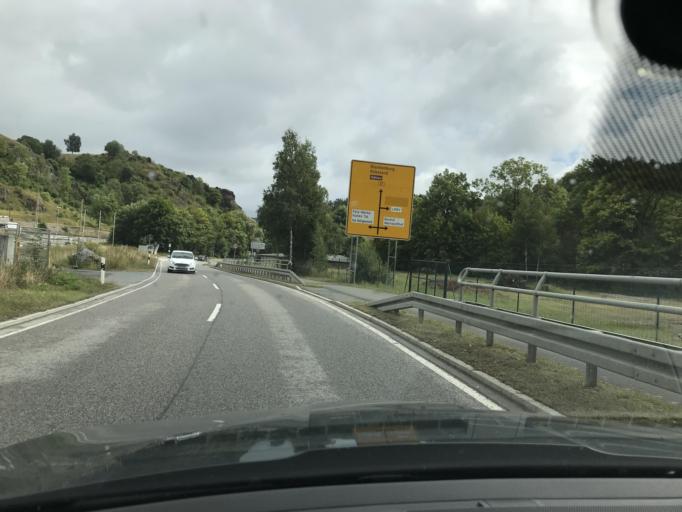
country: DE
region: Saxony-Anhalt
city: Elbingerode
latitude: 51.7653
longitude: 10.8263
